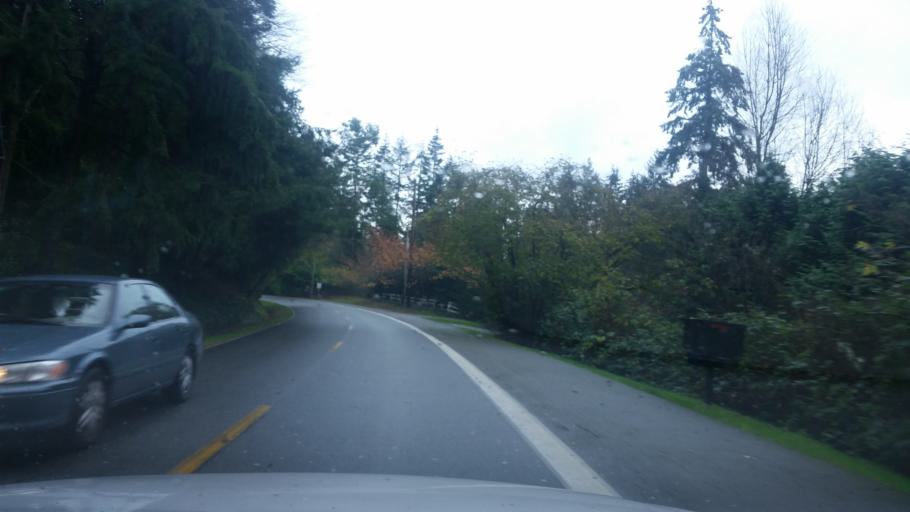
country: US
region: Washington
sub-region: Snohomish County
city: Woodway
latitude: 47.7952
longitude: -122.3838
